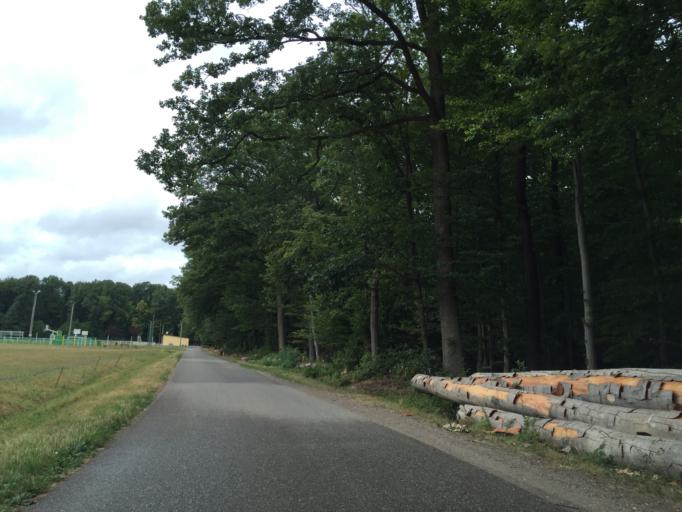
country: FR
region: Alsace
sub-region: Departement du Bas-Rhin
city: Soultz-sous-Forets
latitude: 48.9603
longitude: 7.9051
